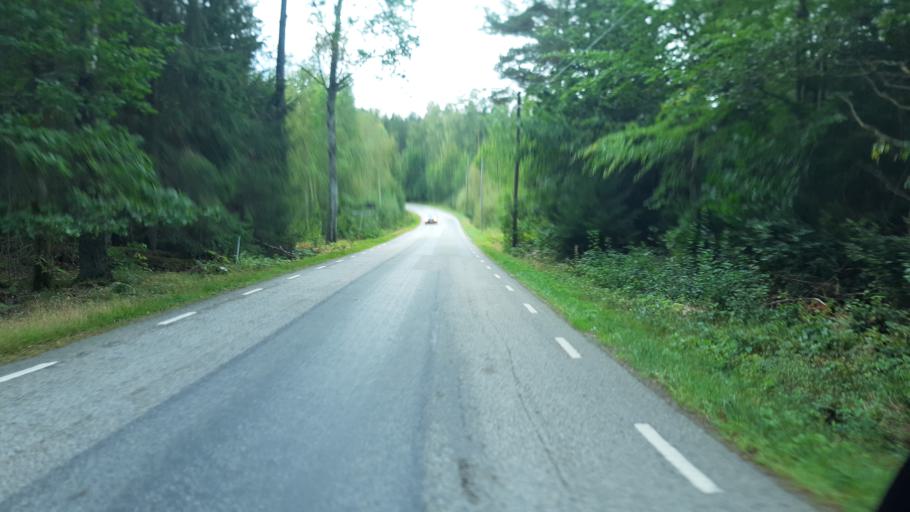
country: SE
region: Blekinge
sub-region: Ronneby Kommun
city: Brakne-Hoby
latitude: 56.3554
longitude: 15.1619
